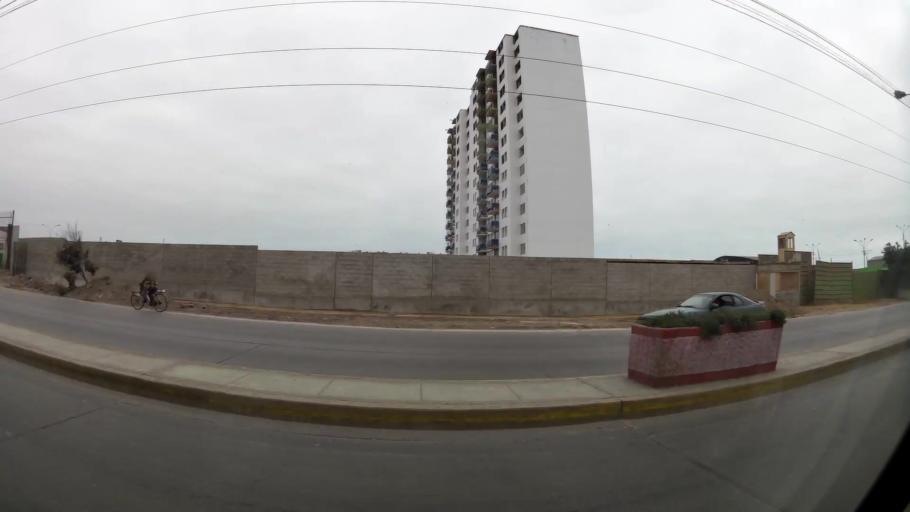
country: PE
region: Callao
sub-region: Callao
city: Callao
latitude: -12.0500
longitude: -77.1160
